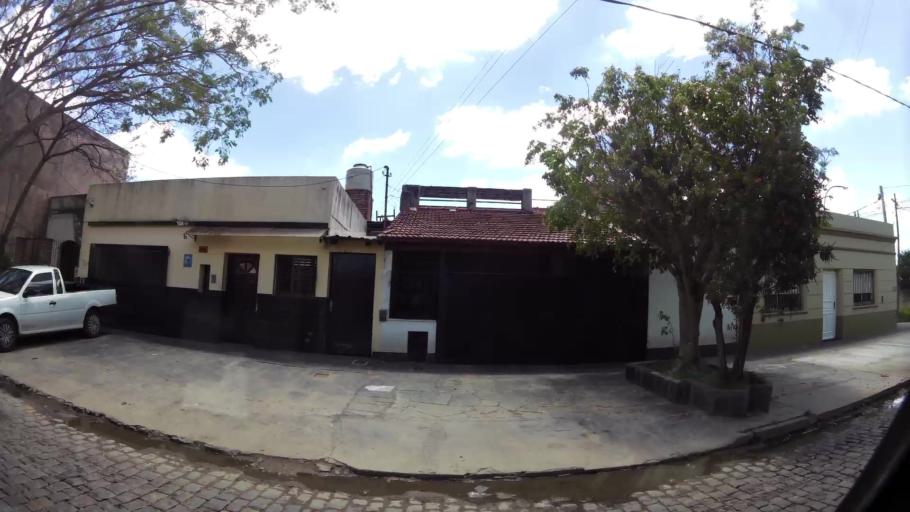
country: AR
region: Buenos Aires
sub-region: Partido de Lomas de Zamora
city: Lomas de Zamora
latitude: -34.7310
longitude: -58.4103
